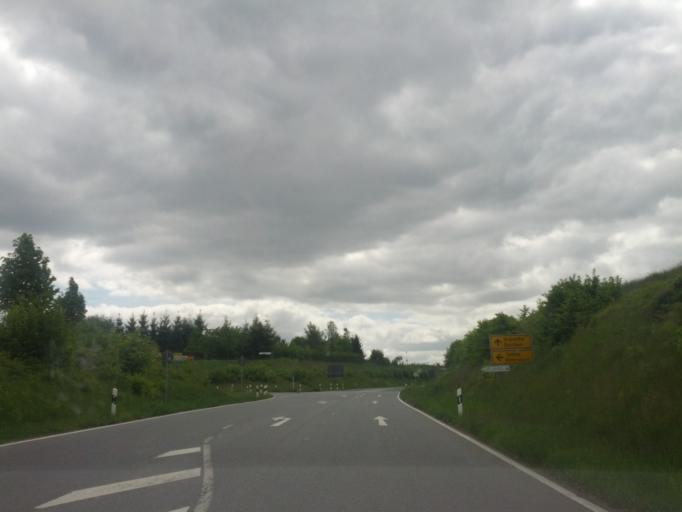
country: DE
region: Saxony
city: Dohna
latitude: 50.9699
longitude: 13.8088
